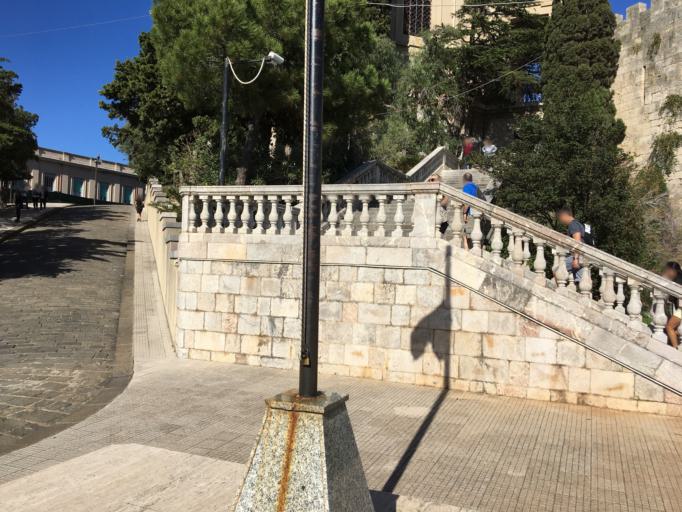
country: IT
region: Sicily
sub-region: Messina
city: Messina
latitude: 38.1960
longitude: 15.5519
